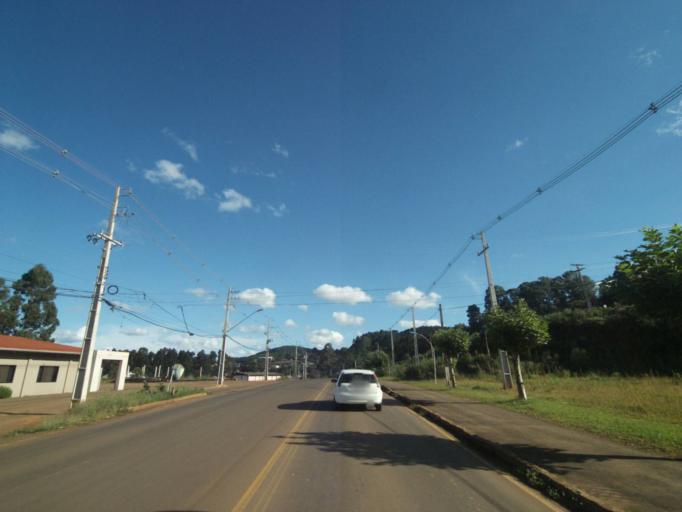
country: BR
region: Parana
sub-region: Uniao Da Vitoria
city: Uniao da Vitoria
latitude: -26.1560
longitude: -51.5421
